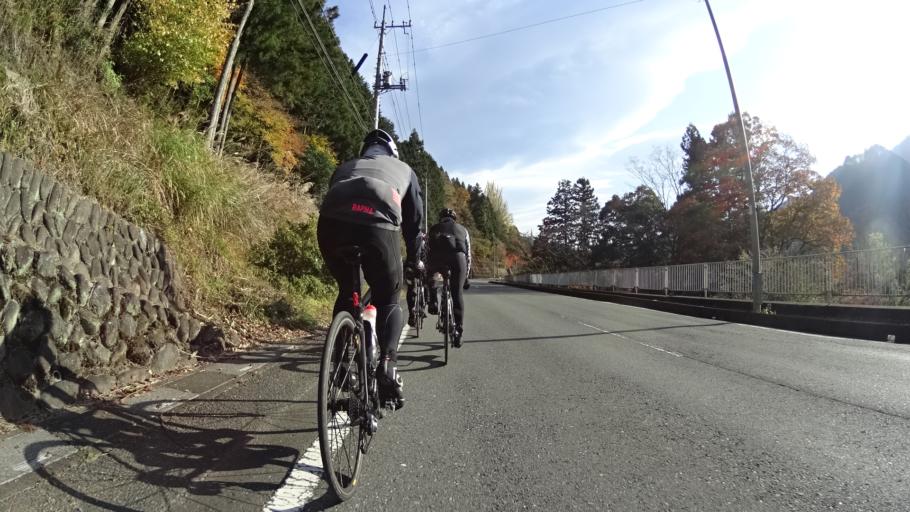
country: JP
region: Tokyo
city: Ome
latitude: 35.8875
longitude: 139.1814
